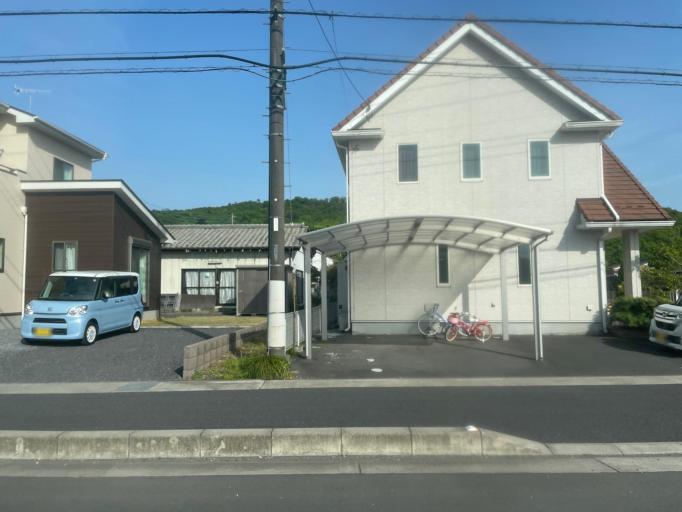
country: JP
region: Tochigi
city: Ashikaga
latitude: 36.3235
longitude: 139.4992
